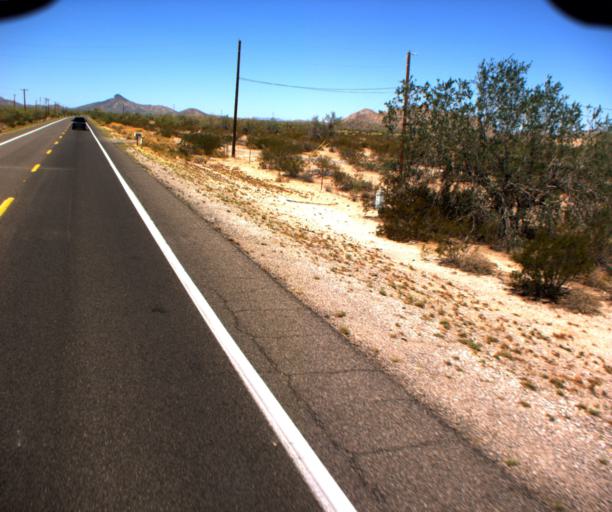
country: US
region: Arizona
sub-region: Pinal County
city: Maricopa
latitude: 32.8496
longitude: -112.0909
